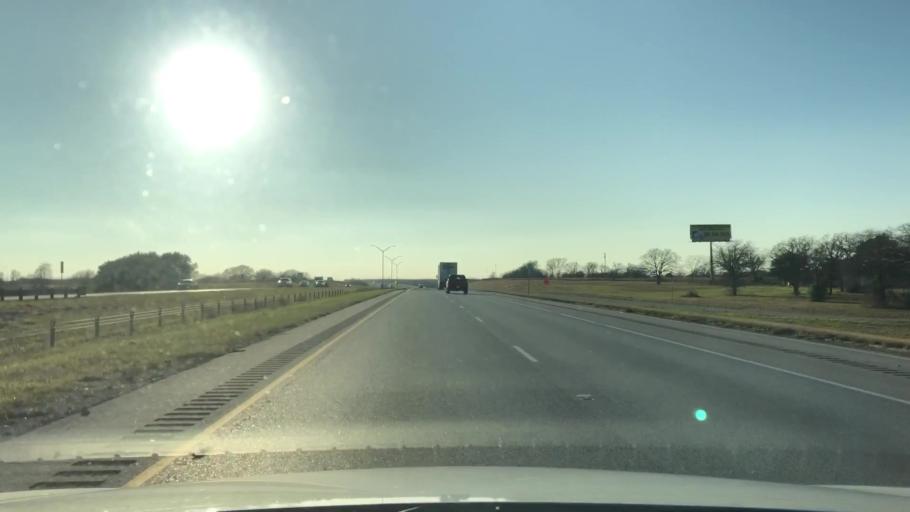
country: US
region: Texas
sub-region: Gonzales County
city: Waelder
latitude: 29.6887
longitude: -97.2540
